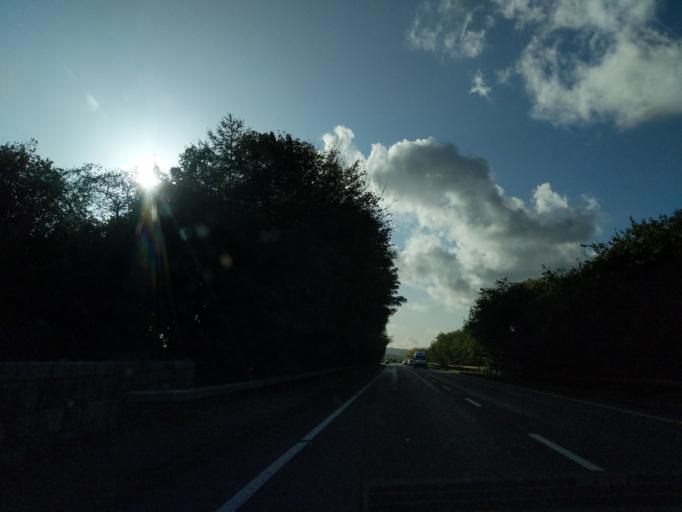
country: GB
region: Scotland
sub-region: Dumfries and Galloway
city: Castle Douglas
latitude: 54.9216
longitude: -3.9719
